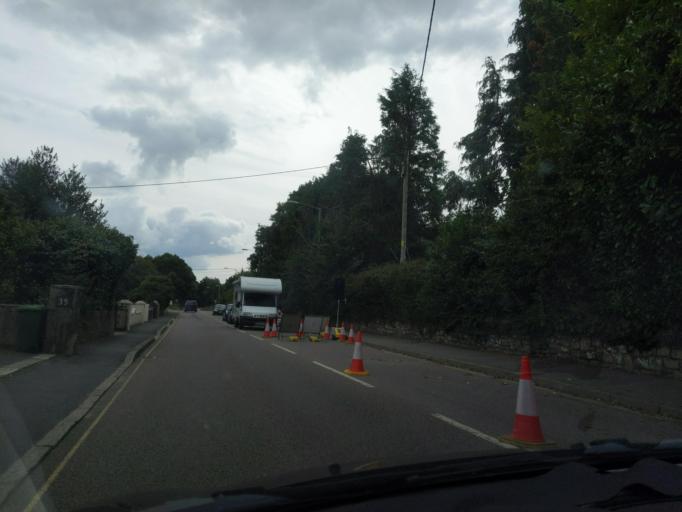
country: GB
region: England
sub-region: Cornwall
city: St Austell
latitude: 50.3322
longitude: -4.7927
